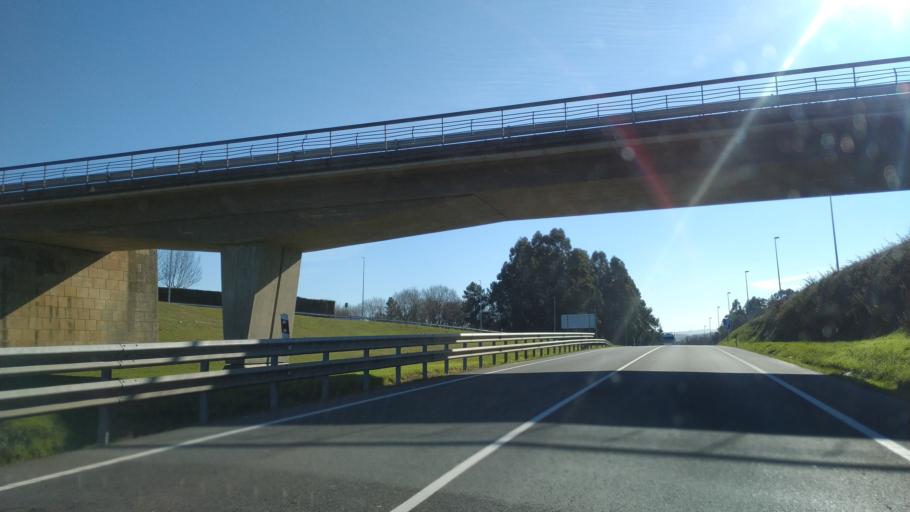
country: ES
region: Galicia
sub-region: Provincia de Pontevedra
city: Silleda
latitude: 42.6930
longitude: -8.2257
